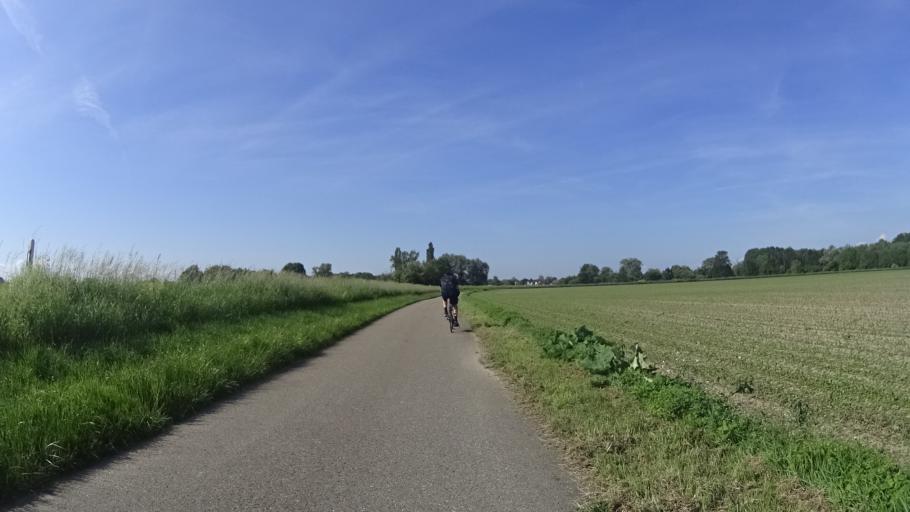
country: DE
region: Baden-Wuerttemberg
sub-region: Freiburg Region
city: Kehl
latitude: 48.5325
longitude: 7.8310
